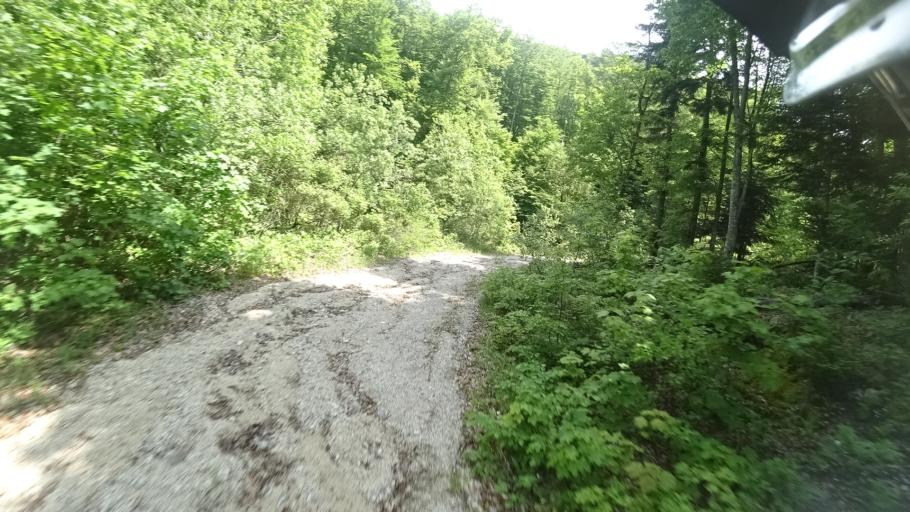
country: BA
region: Federation of Bosnia and Herzegovina
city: Orasac
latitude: 44.5647
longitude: 15.8662
